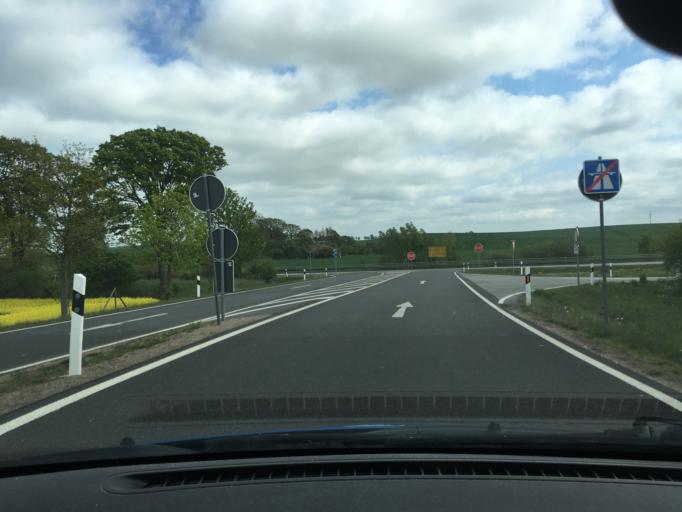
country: DE
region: Mecklenburg-Vorpommern
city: Leezen
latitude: 53.6914
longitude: 11.5099
